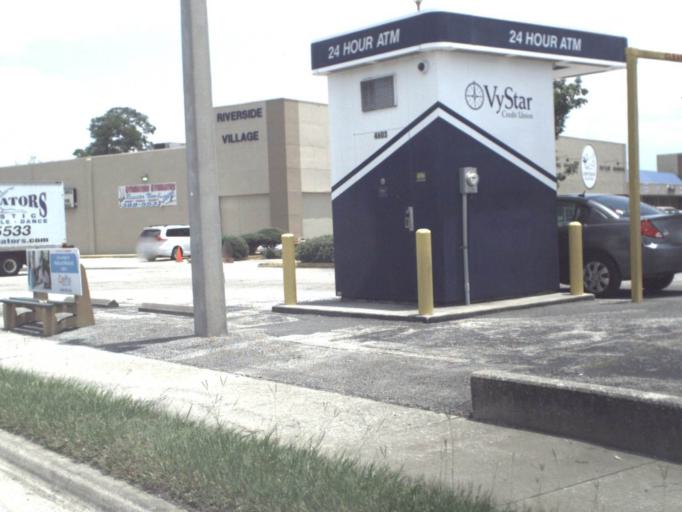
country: US
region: Florida
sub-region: Duval County
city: Jacksonville
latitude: 30.2842
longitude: -81.7251
